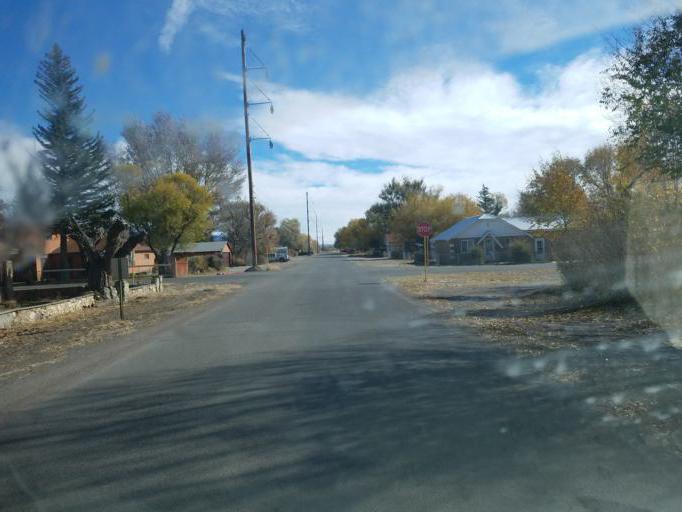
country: US
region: Colorado
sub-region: Alamosa County
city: Alamosa
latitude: 37.4709
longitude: -105.8565
